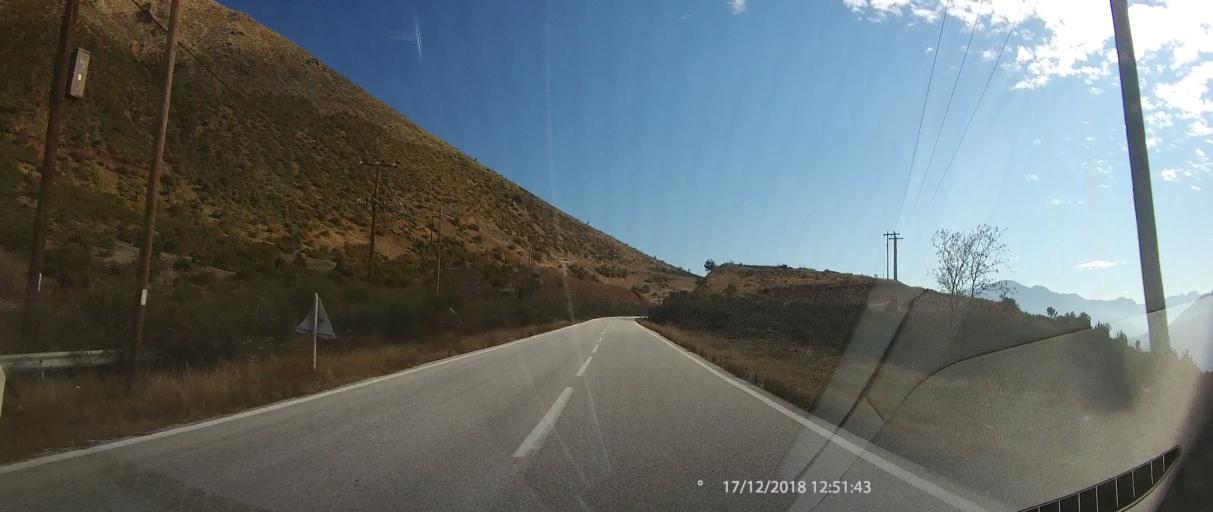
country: GR
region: Thessaly
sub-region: Trikala
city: Kastraki
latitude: 39.7635
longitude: 21.4700
